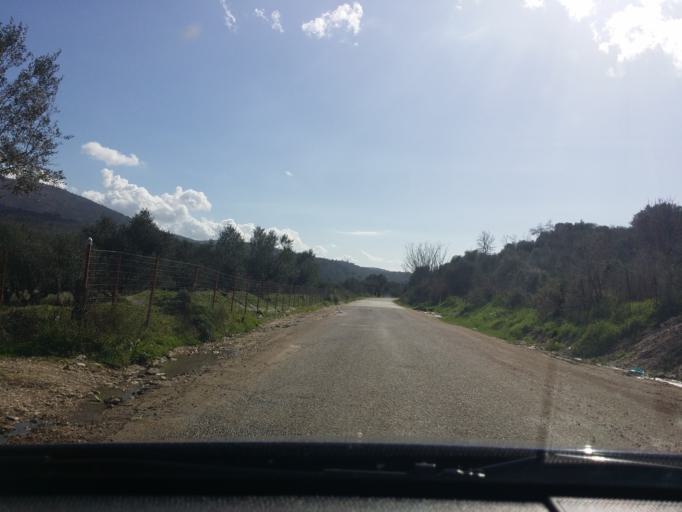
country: GR
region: West Greece
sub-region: Nomos Aitolias kai Akarnanias
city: Astakos
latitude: 38.5603
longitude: 21.0968
